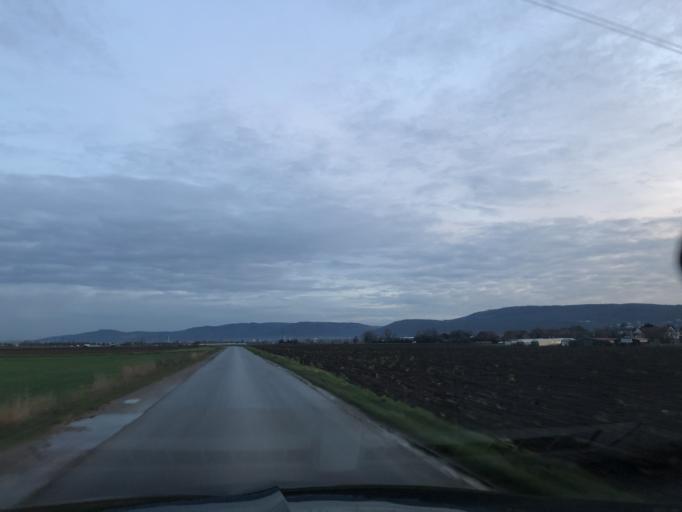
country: DE
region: Baden-Wuerttemberg
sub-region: Karlsruhe Region
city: Sandhausen
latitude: 49.3583
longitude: 8.6349
